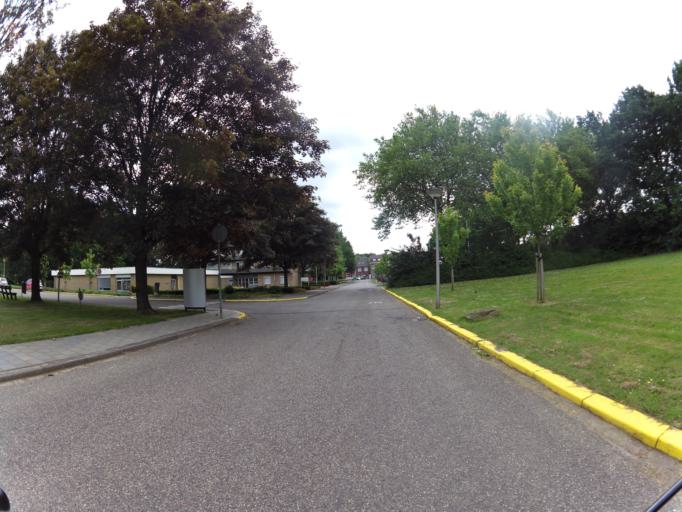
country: NL
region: Limburg
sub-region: Gemeente Kerkrade
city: Kerkrade
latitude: 50.8791
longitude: 6.0606
